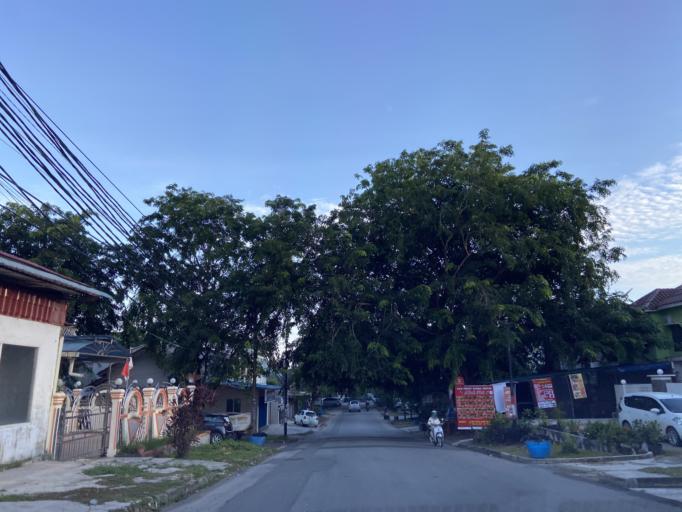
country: SG
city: Singapore
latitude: 1.1214
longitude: 104.0419
